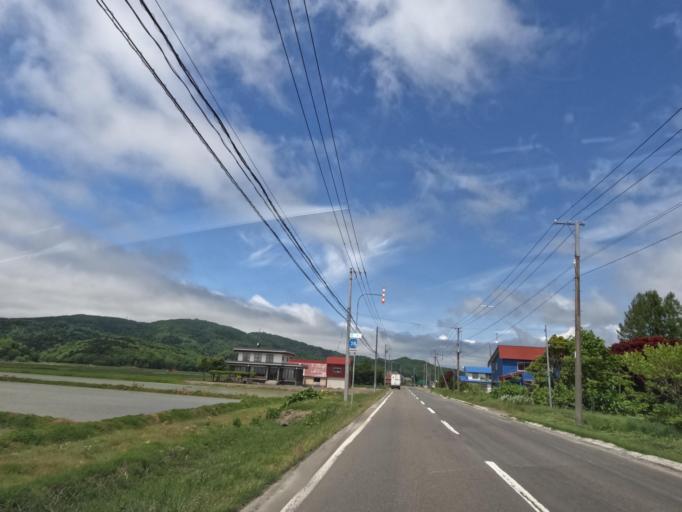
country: JP
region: Hokkaido
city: Tobetsu
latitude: 43.2768
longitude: 141.5343
